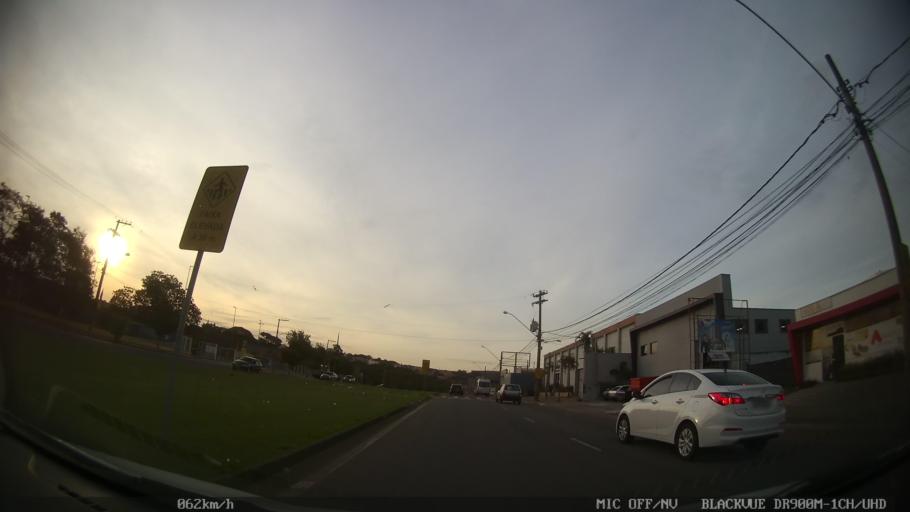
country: BR
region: Sao Paulo
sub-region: Limeira
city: Limeira
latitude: -22.5660
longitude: -47.3804
